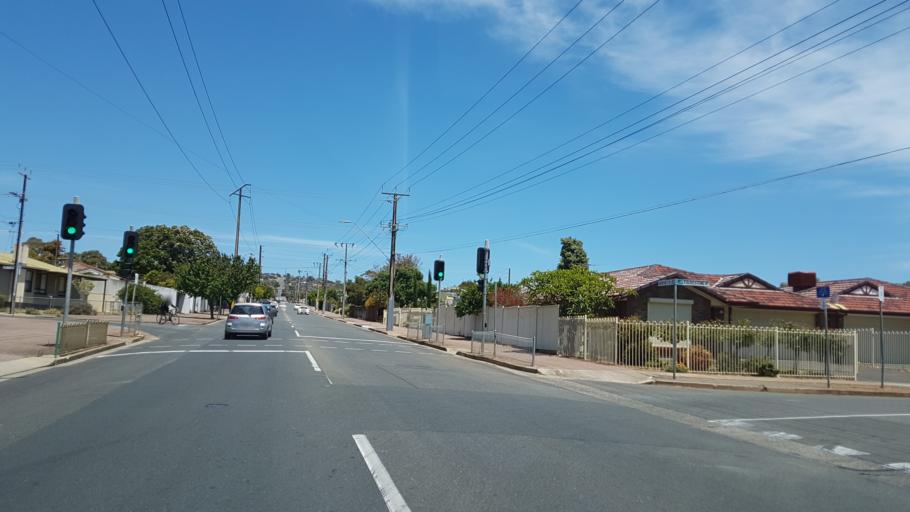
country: AU
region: South Australia
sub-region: Holdfast Bay
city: Seacliff Park
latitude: -35.0252
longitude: 138.5416
